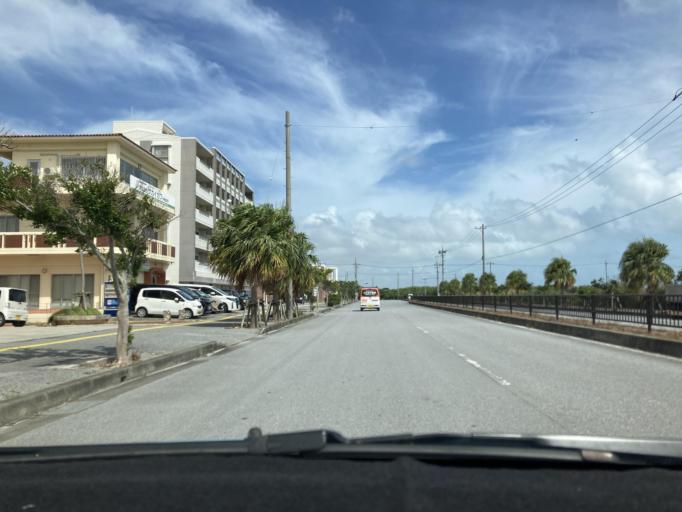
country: JP
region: Okinawa
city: Ginowan
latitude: 26.2080
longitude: 127.7634
